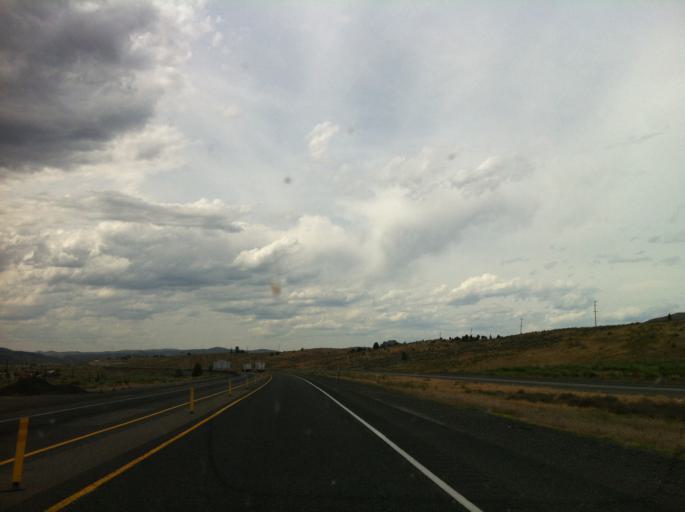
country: US
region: Oregon
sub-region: Baker County
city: Baker City
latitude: 44.5531
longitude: -117.4241
